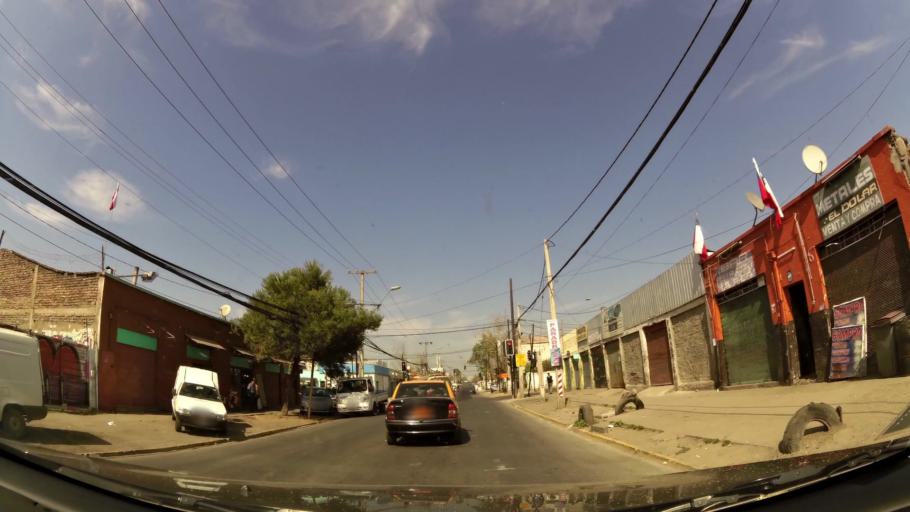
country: CL
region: Santiago Metropolitan
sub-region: Provincia de Santiago
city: Santiago
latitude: -33.3991
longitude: -70.6285
